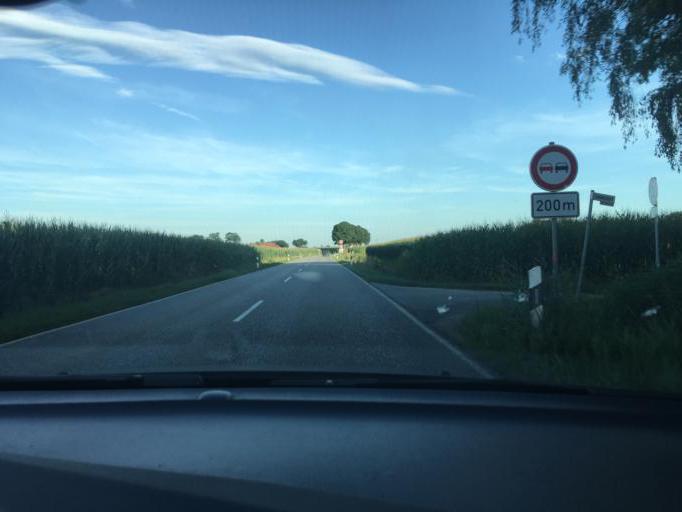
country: DE
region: Bavaria
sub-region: Upper Bavaria
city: Erding
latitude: 48.3004
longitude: 11.9273
